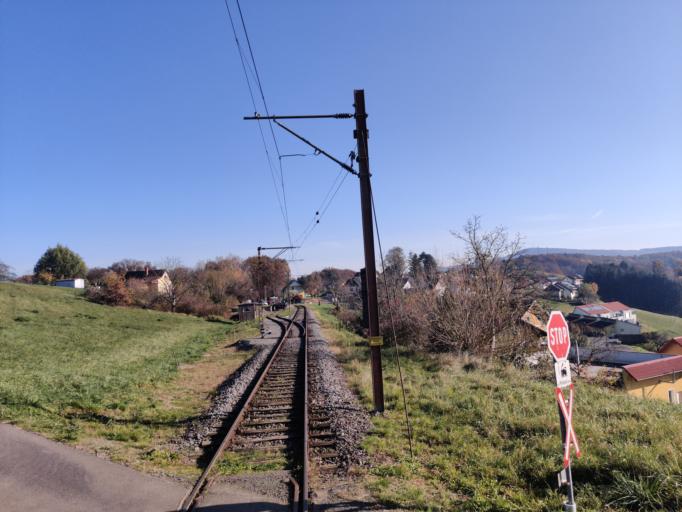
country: AT
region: Styria
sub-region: Politischer Bezirk Suedoststeiermark
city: Trautmannsdorf in Oststeiermark
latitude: 46.8786
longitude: 15.8866
